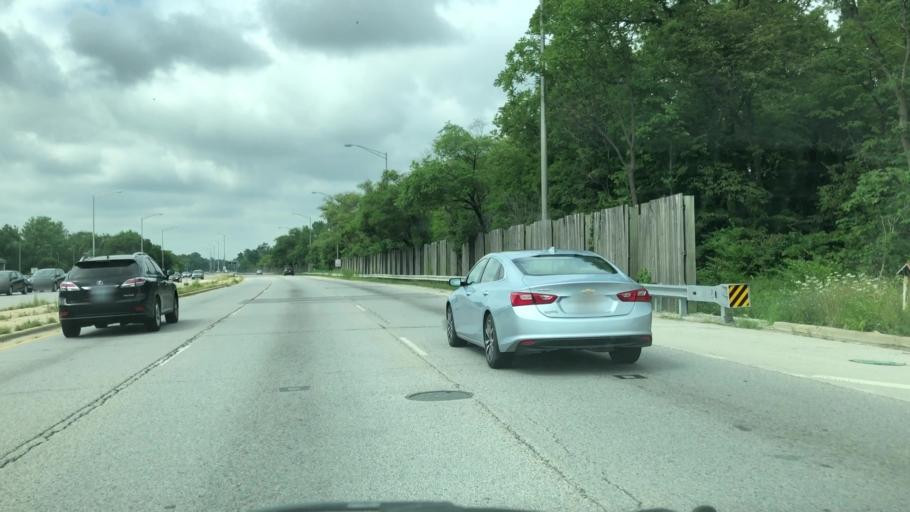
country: US
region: Illinois
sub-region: DuPage County
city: Elmhurst
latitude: 41.9068
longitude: -87.9649
